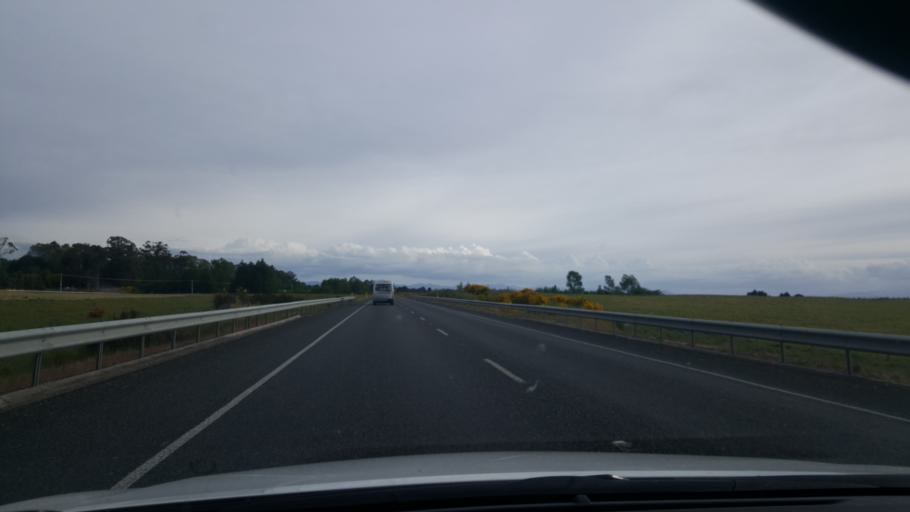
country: NZ
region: Waikato
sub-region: Taupo District
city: Taupo
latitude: -38.6554
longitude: 176.1006
